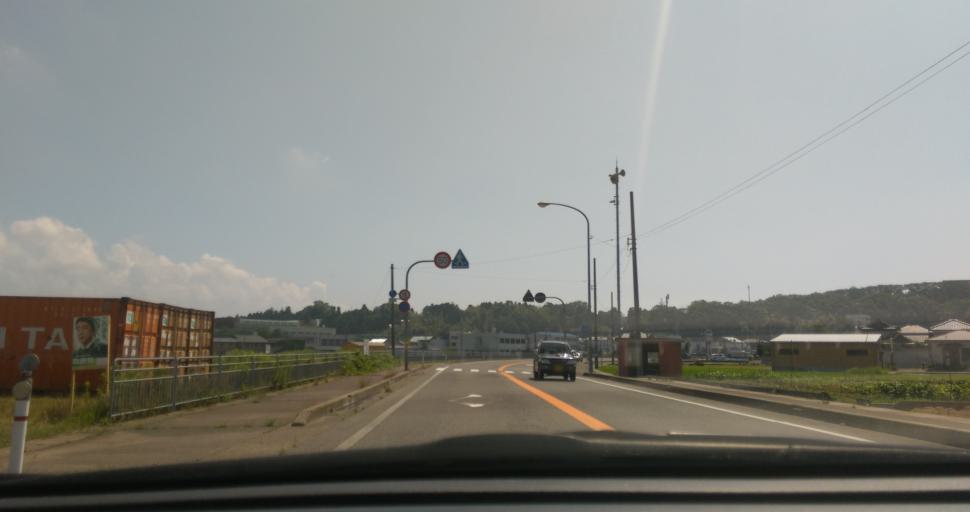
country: JP
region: Fukui
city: Mikuni
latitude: 36.2228
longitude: 136.1608
